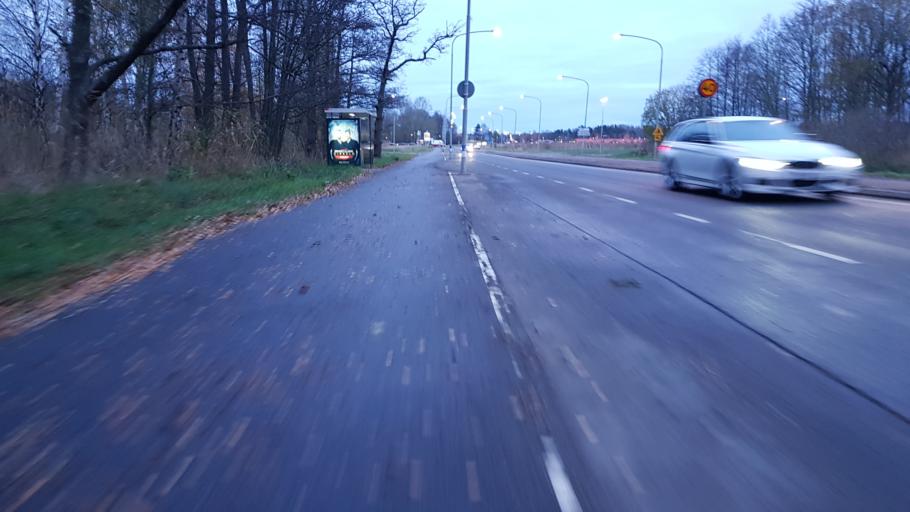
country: SE
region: OEstergoetland
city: Lindo
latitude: 58.5992
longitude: 16.2409
